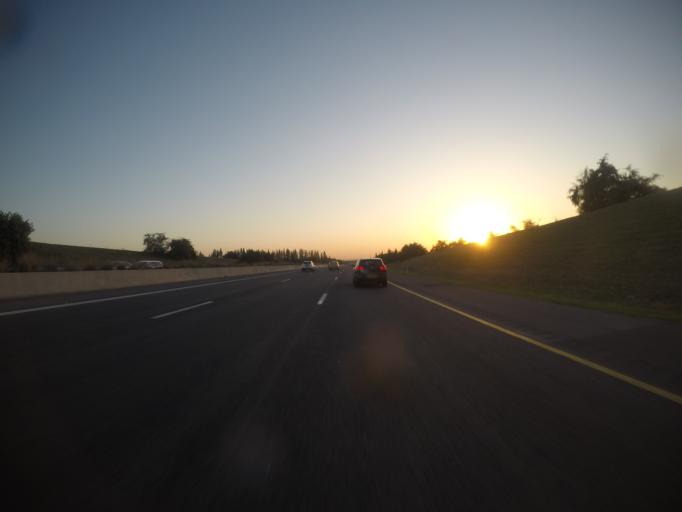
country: PS
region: West Bank
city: Nazlat `Isa
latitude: 32.4412
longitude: 35.0334
